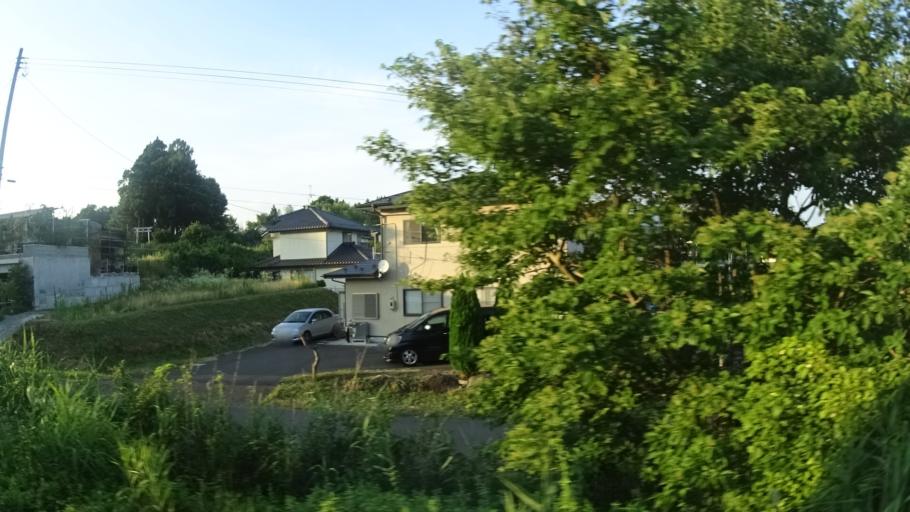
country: JP
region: Fukushima
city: Funehikimachi-funehiki
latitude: 37.4466
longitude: 140.5678
